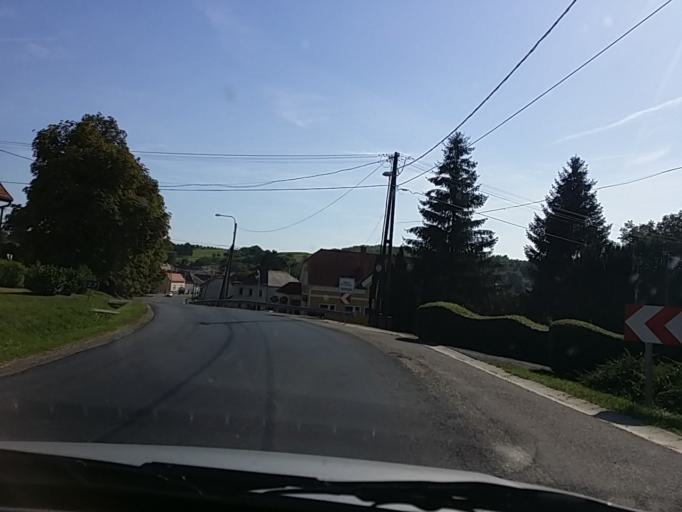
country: AT
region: Burgenland
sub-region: Politischer Bezirk Oberpullendorf
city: Lutzmannsburg
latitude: 47.4274
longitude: 16.6498
